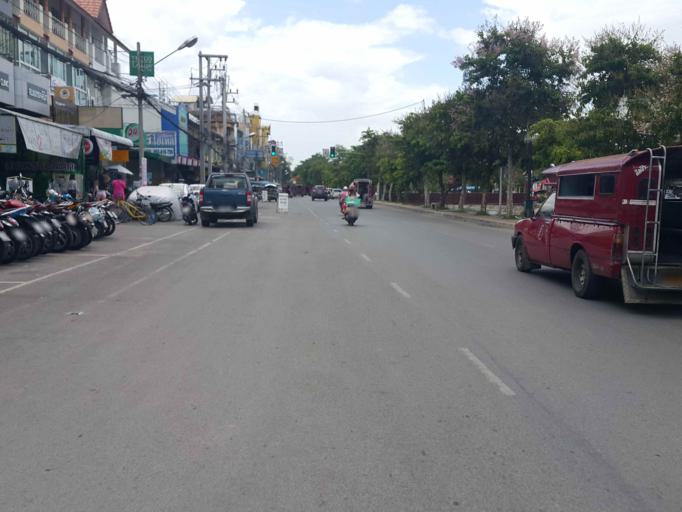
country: TH
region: Chiang Mai
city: Chiang Mai
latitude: 18.7907
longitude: 98.9934
